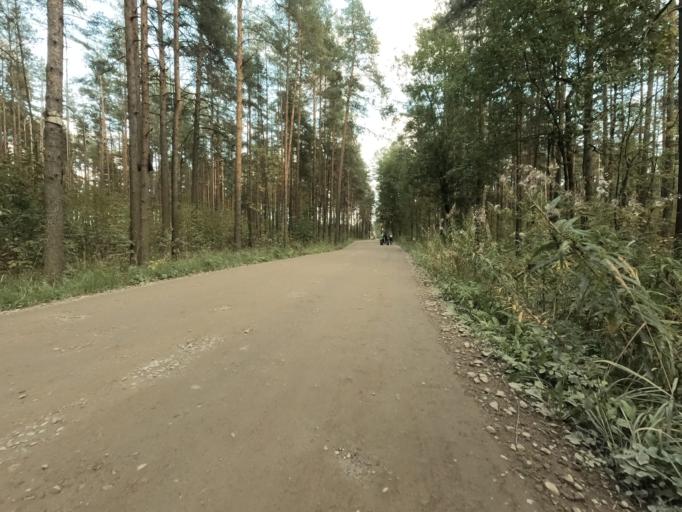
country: RU
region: Leningrad
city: Imeni Sverdlova
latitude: 59.8401
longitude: 30.7005
